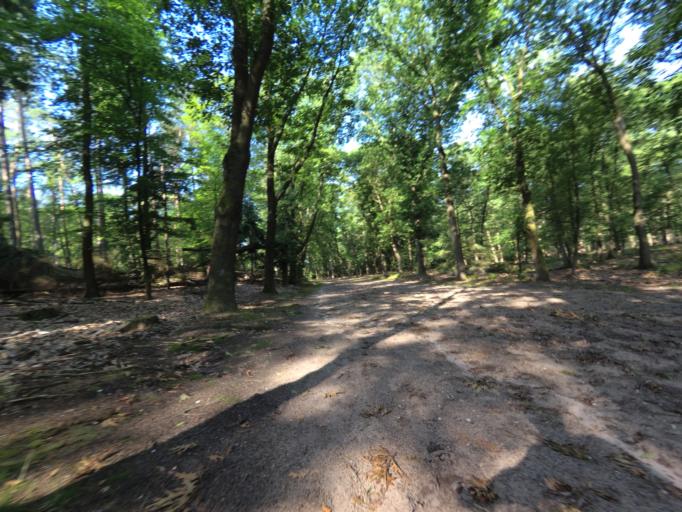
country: NL
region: Gelderland
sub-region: Gemeente Apeldoorn
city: Beekbergen
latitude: 52.1771
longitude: 5.9018
